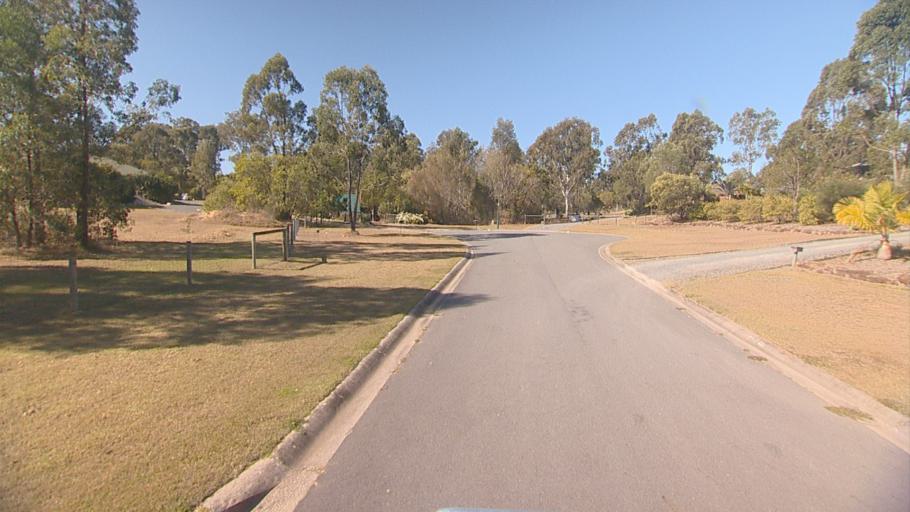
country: AU
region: Queensland
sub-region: Logan
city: Cedar Vale
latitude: -27.8595
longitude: 153.0422
